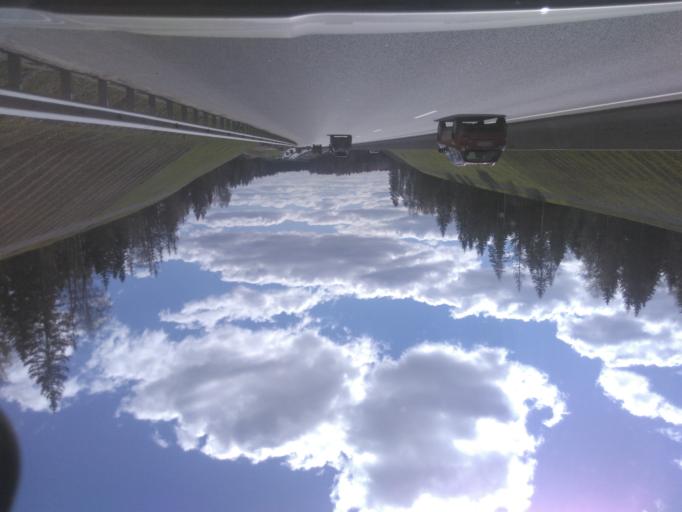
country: RU
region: Moskovskaya
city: Rzhavki
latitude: 56.0413
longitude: 37.2672
